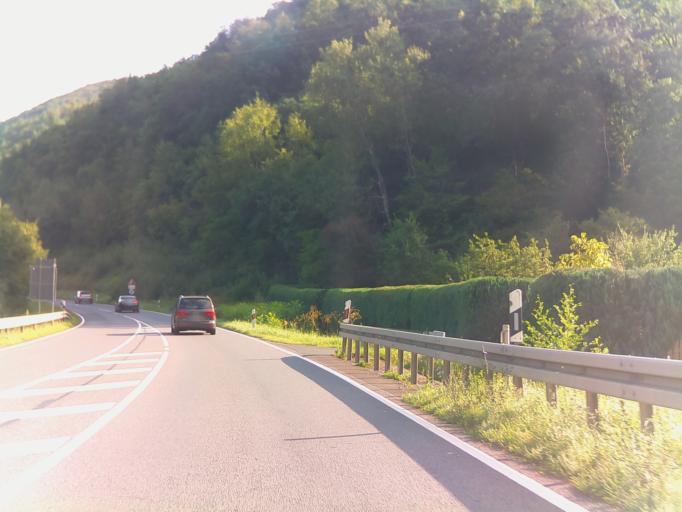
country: DE
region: Bavaria
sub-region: Regierungsbezirk Unterfranken
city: Neuendorf
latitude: 50.0558
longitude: 9.6418
